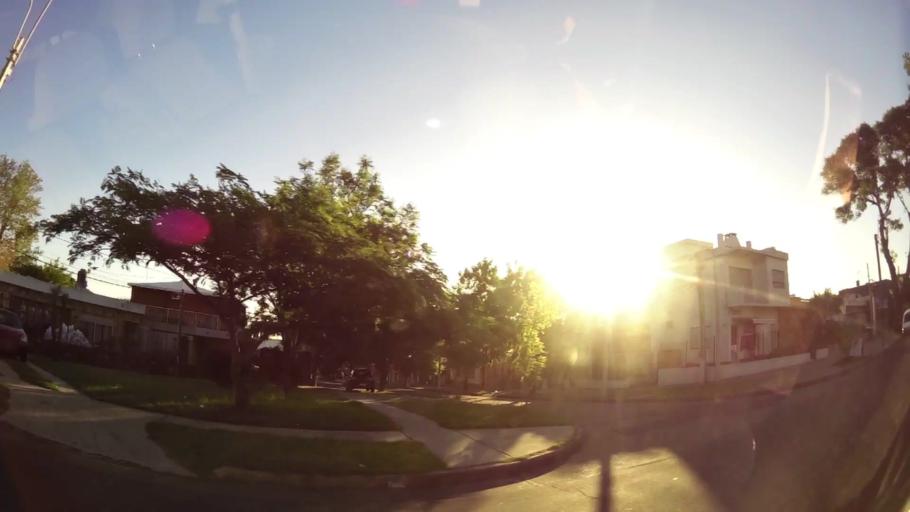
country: UY
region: Montevideo
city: Montevideo
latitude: -34.8463
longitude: -56.2085
